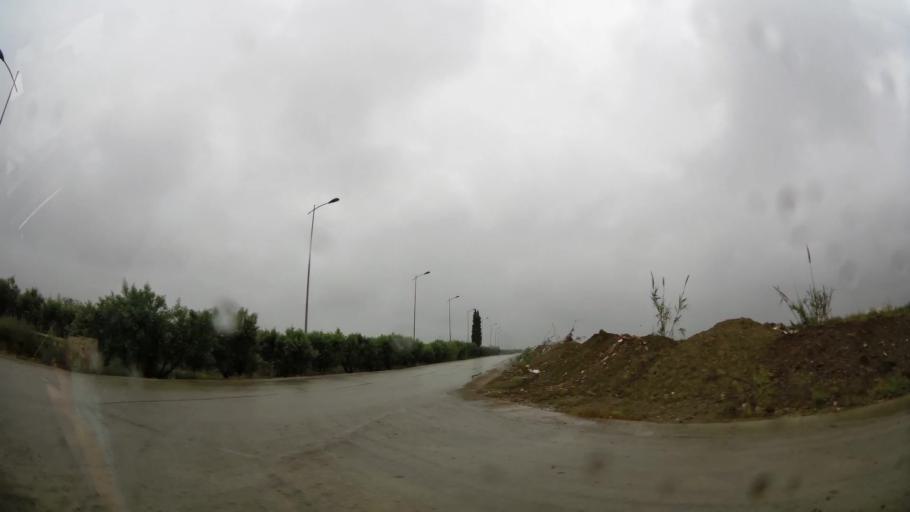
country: MA
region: Taza-Al Hoceima-Taounate
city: Imzourene
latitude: 35.1534
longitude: -3.8225
